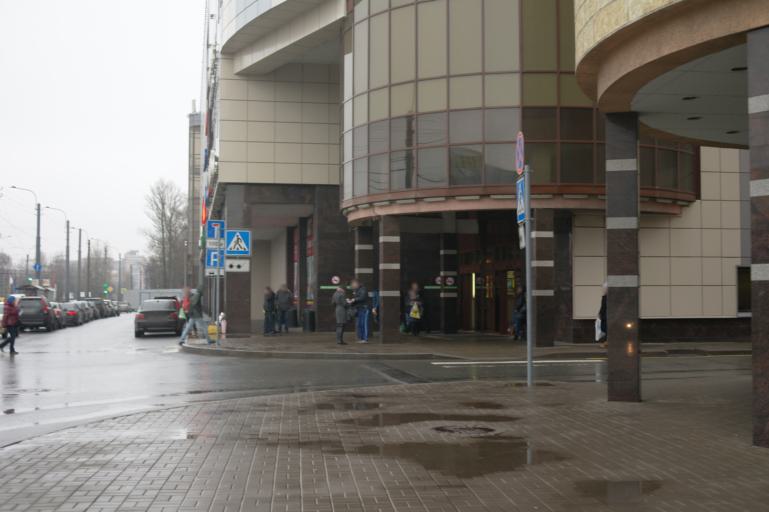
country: RU
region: St.-Petersburg
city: Staraya Derevnya
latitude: 59.9891
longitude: 30.2563
